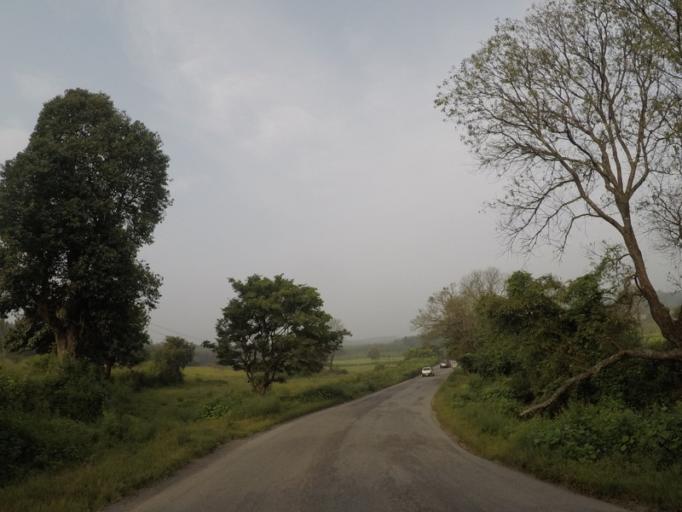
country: IN
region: Karnataka
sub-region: Chikmagalur
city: Chikmagalur
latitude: 13.2675
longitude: 75.7159
